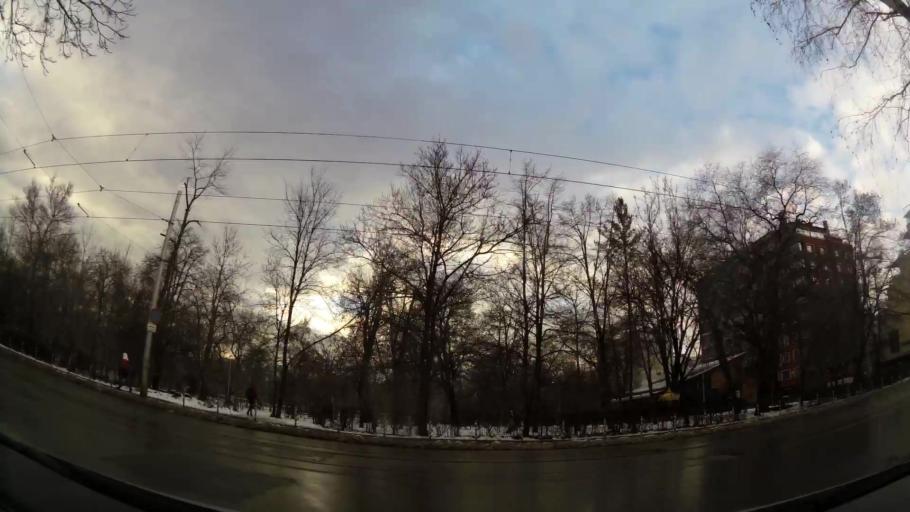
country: BG
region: Sofia-Capital
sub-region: Stolichna Obshtina
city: Sofia
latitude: 42.7058
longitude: 23.2947
